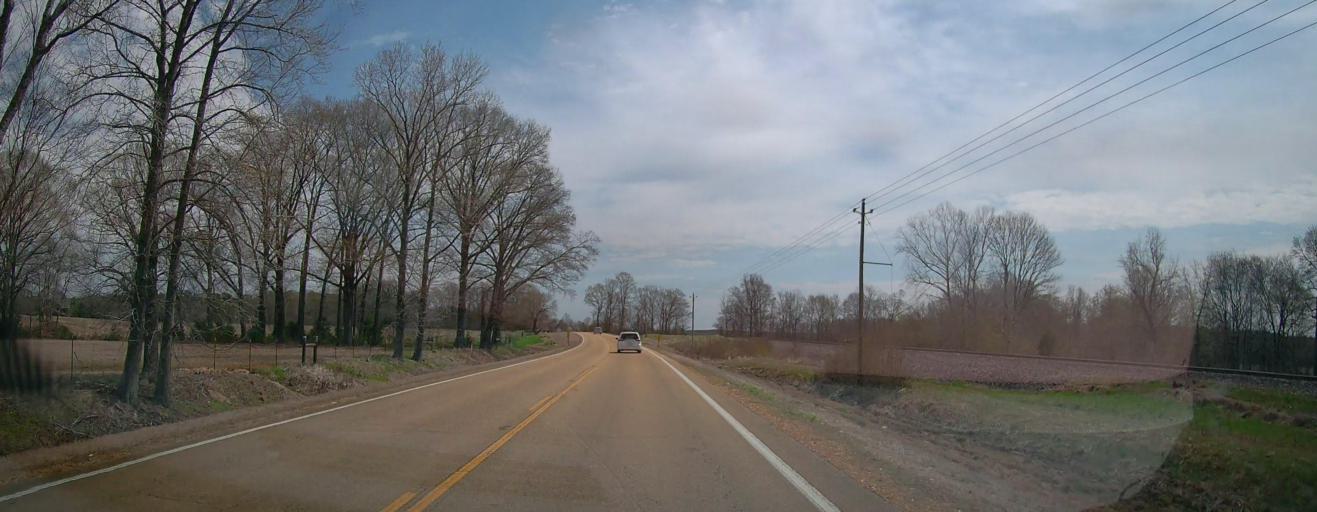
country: US
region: Mississippi
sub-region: Benton County
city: Ashland
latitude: 34.6195
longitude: -89.2250
